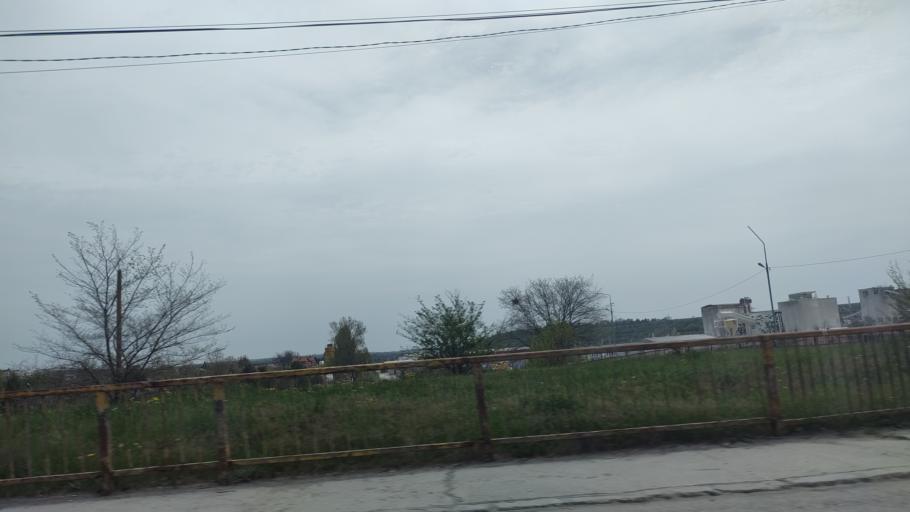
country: RO
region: Constanta
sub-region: Oras Murfatlar
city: Murfatlar
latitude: 44.1713
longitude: 28.4102
